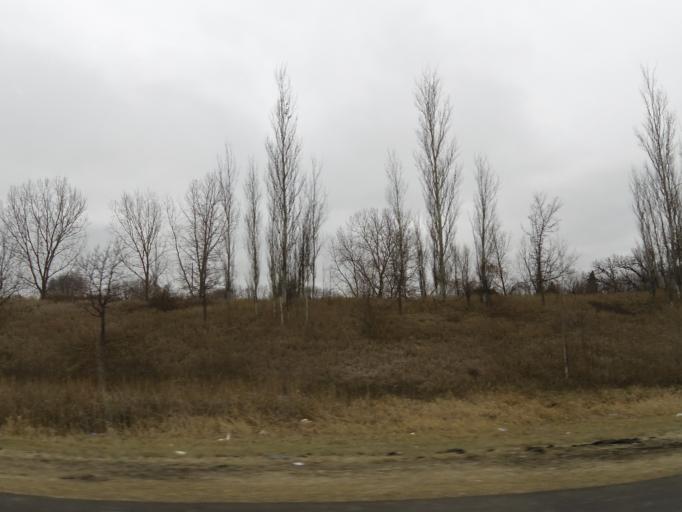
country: US
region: Minnesota
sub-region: Dakota County
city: Eagan
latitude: 44.7991
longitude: -93.1950
